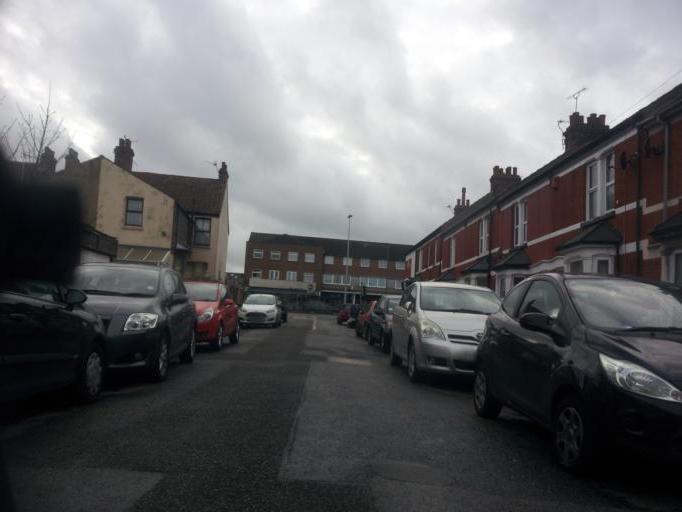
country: GB
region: England
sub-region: Kent
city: Gillingham
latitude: 51.3740
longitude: 0.5538
